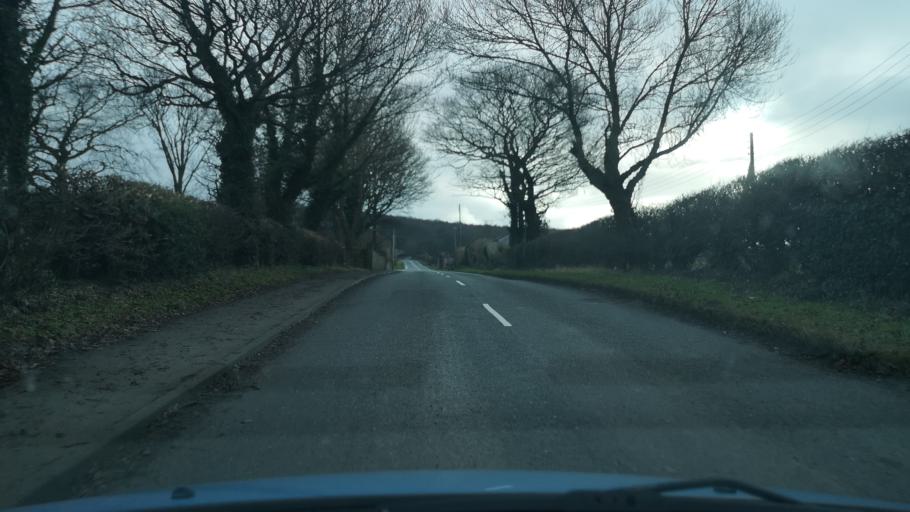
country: GB
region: England
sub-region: City and Borough of Wakefield
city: Crigglestone
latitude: 53.6256
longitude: -1.5388
